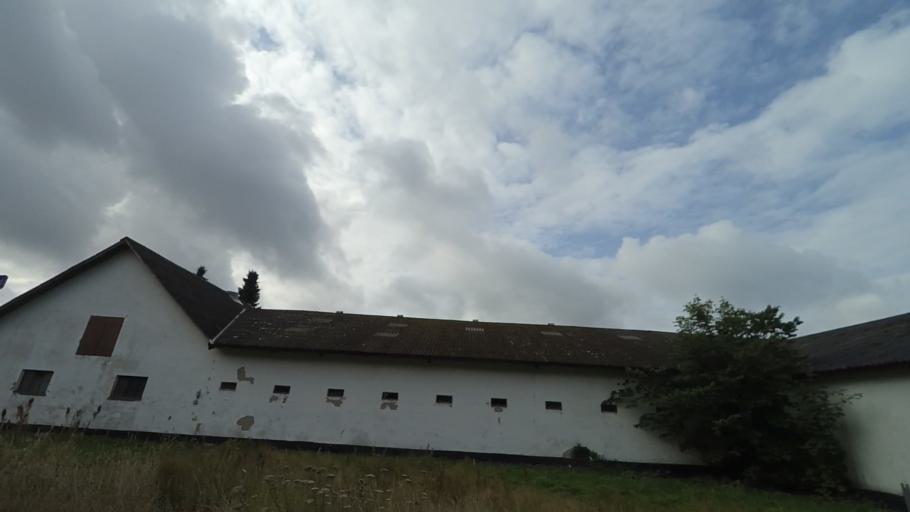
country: DK
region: Central Jutland
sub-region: Syddjurs Kommune
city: Ryomgard
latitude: 56.3510
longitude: 10.5157
